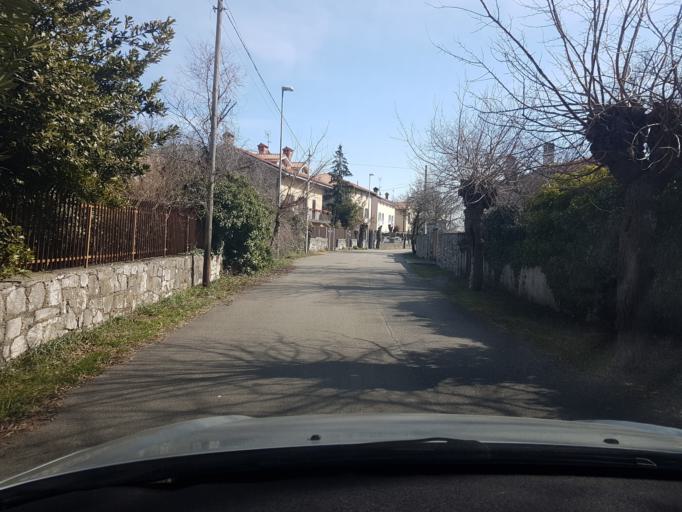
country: IT
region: Friuli Venezia Giulia
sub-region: Provincia di Trieste
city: Aurisina
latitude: 45.7521
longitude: 13.6666
